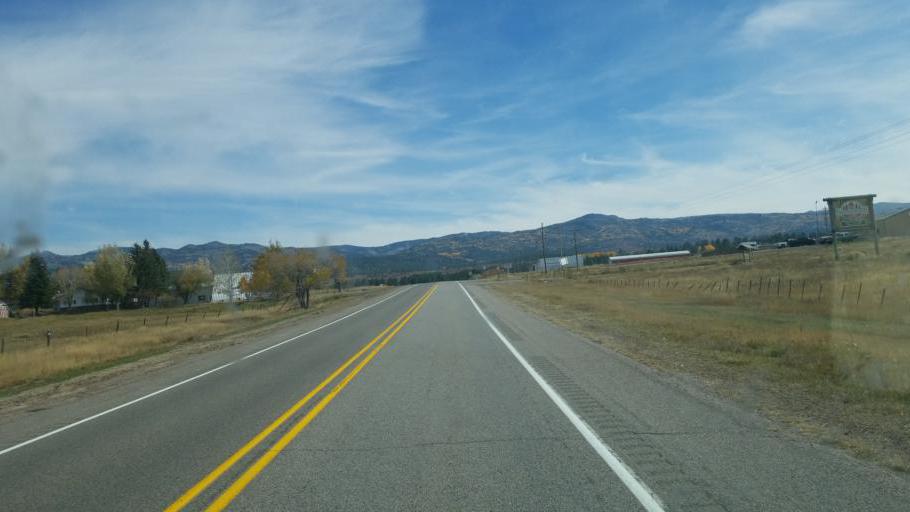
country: US
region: New Mexico
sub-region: Rio Arriba County
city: Chama
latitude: 36.8831
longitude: -106.5939
